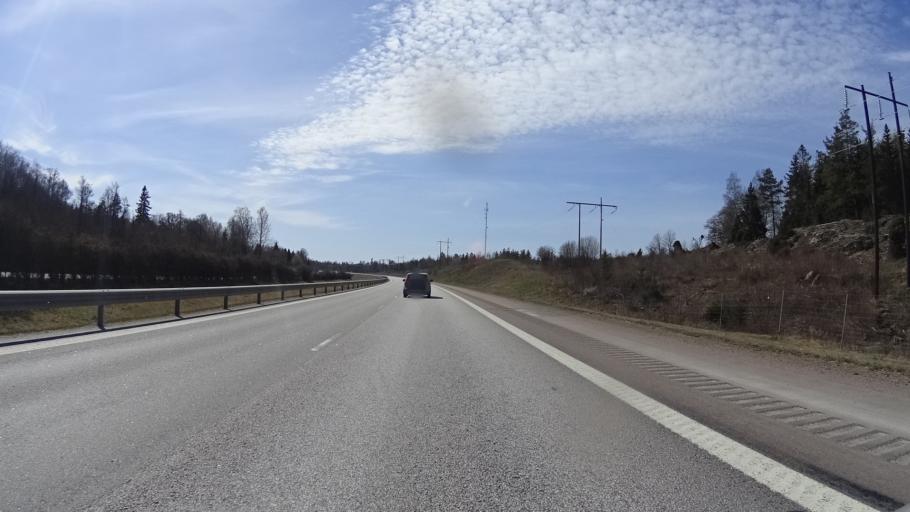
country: SE
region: OEstergoetland
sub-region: Vadstena Kommun
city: Herrestad
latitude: 58.2876
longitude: 14.8810
